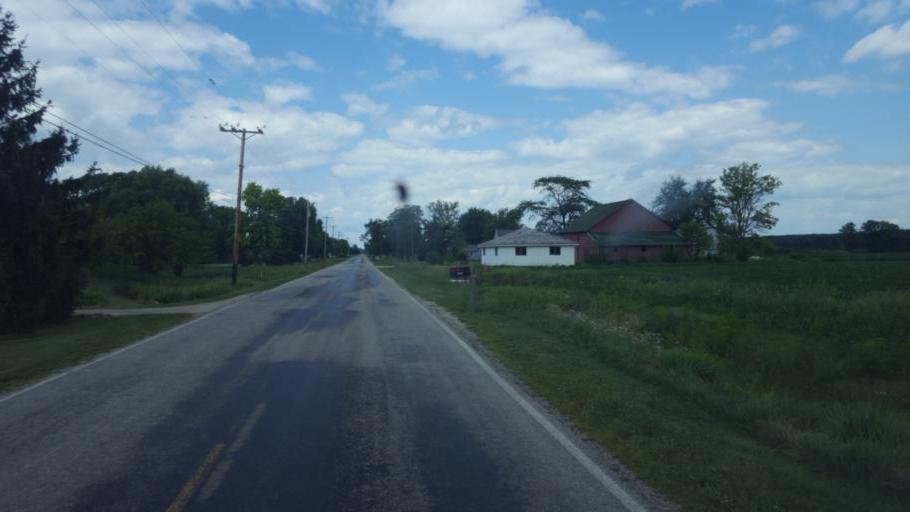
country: US
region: Ohio
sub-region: Lucas County
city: Curtice
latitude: 41.6086
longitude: -83.2794
